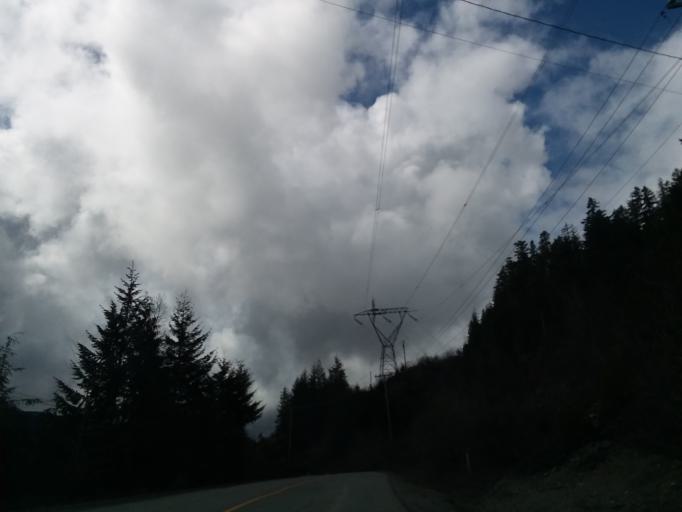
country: CA
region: British Columbia
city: Whistler
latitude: 50.0990
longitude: -123.0012
